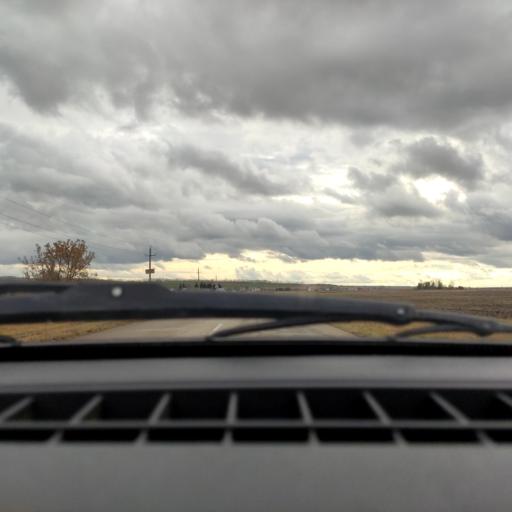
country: RU
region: Bashkortostan
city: Asanovo
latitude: 54.9328
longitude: 55.5175
